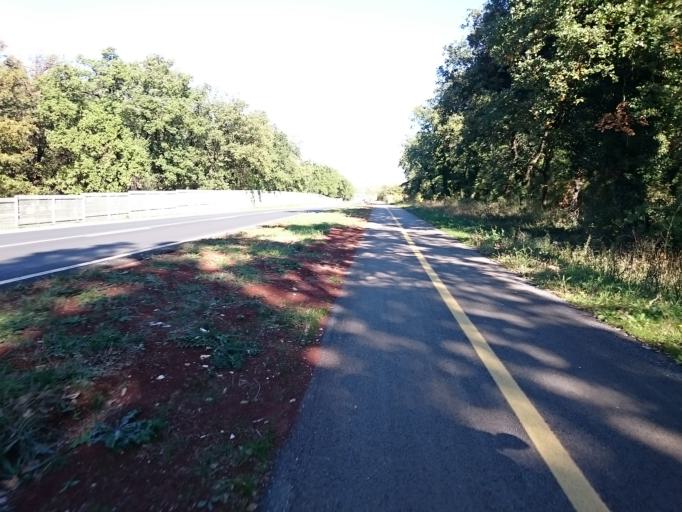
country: HR
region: Istarska
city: Umag
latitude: 45.4169
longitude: 13.5296
